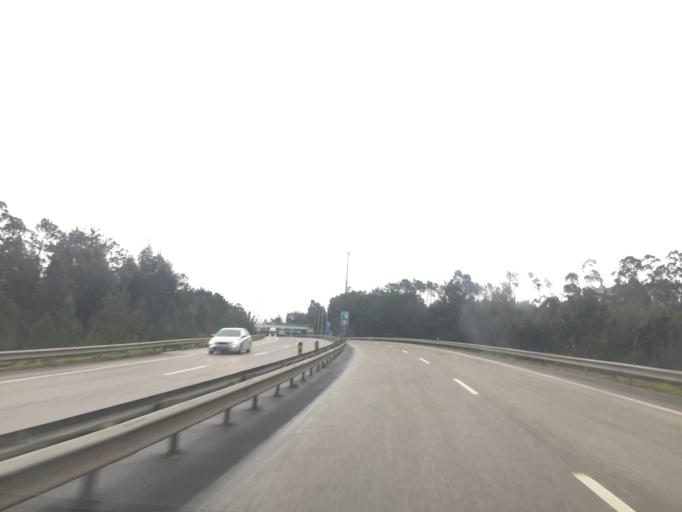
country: PT
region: Leiria
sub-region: Leiria
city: Caranguejeira
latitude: 39.7367
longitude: -8.7497
